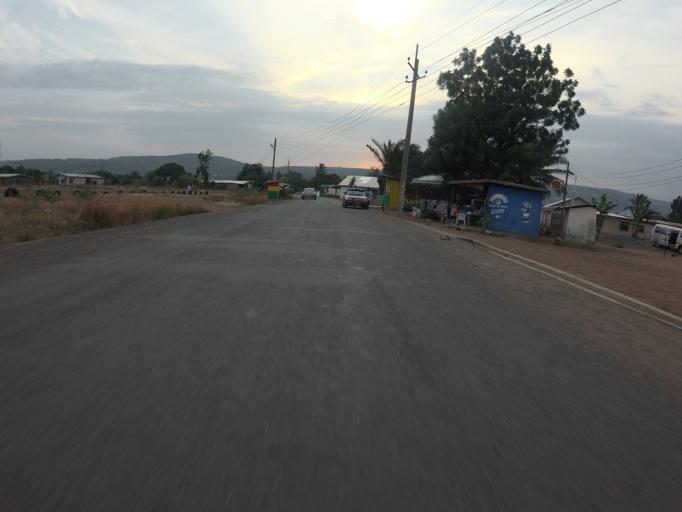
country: GH
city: Akropong
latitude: 6.1016
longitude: -0.0111
